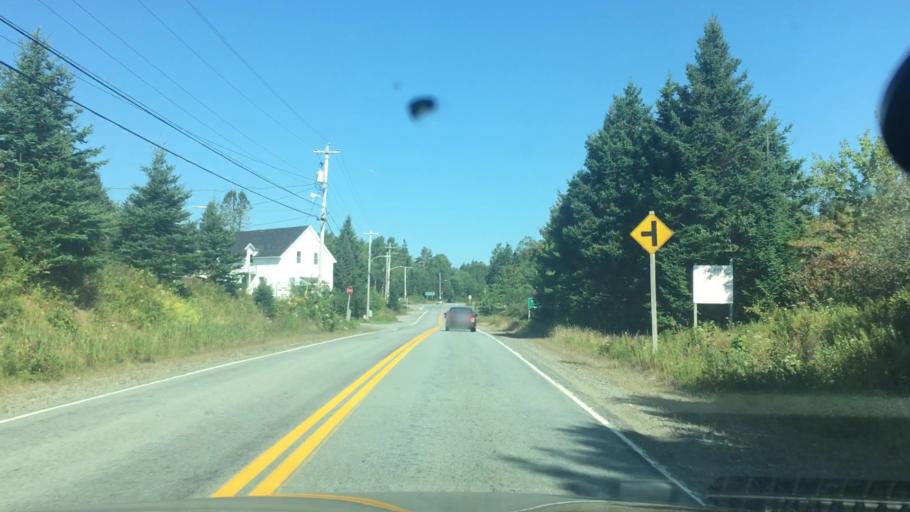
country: CA
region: Nova Scotia
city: New Glasgow
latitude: 44.9241
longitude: -62.5457
